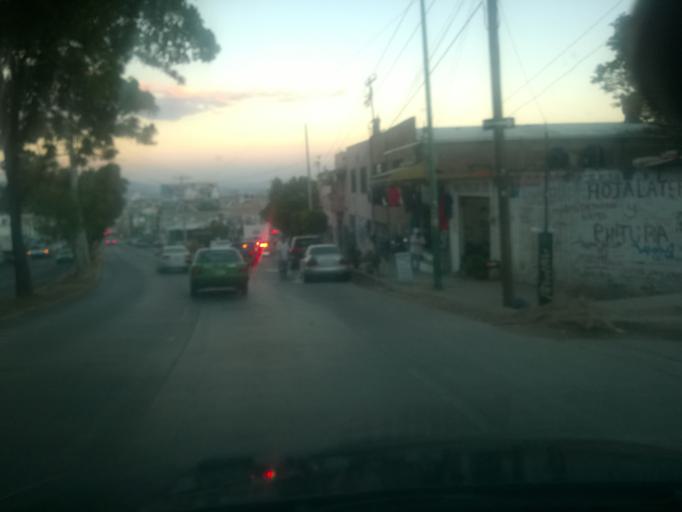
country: MX
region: Guanajuato
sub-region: Leon
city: Ejido la Joya
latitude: 21.1172
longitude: -101.7127
